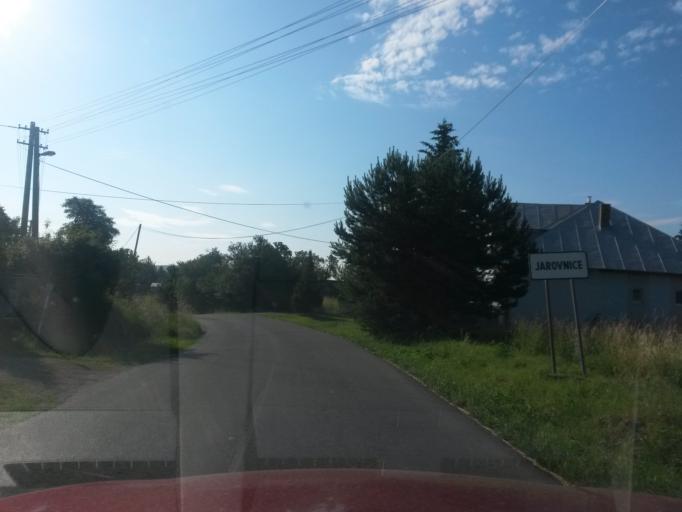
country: SK
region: Presovsky
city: Sabinov
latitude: 49.0637
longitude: 21.0575
